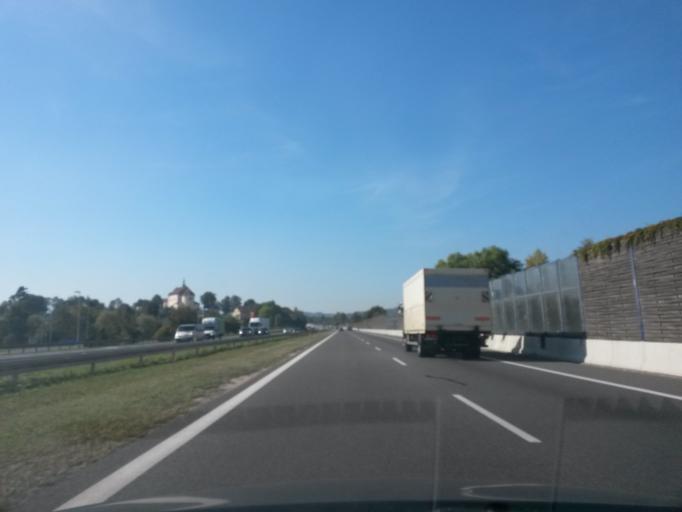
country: PL
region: Lesser Poland Voivodeship
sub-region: Powiat krakowski
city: Balice
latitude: 50.0798
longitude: 19.7593
